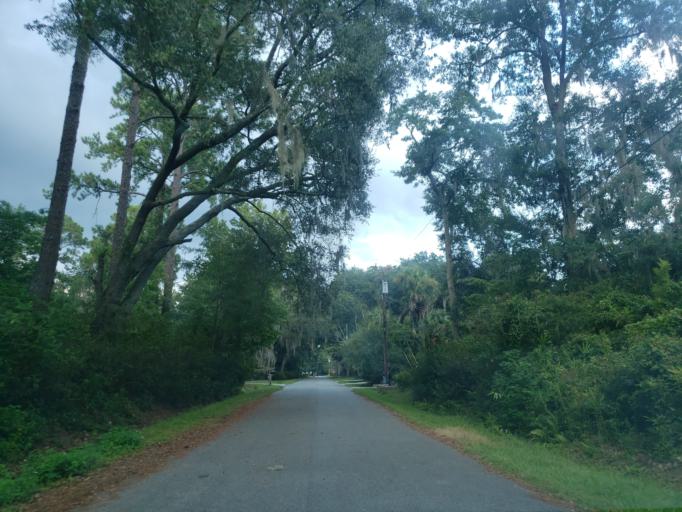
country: US
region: Georgia
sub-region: Chatham County
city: Isle of Hope
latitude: 31.9916
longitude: -81.0656
